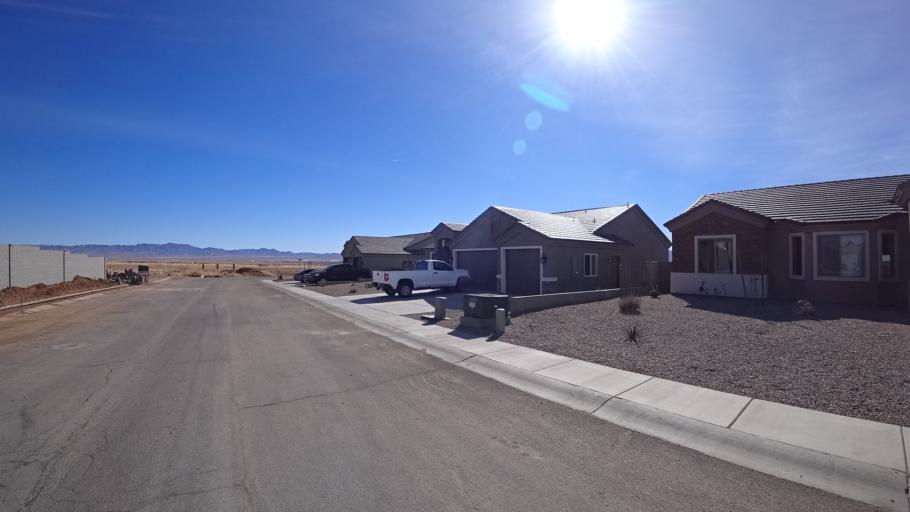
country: US
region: Arizona
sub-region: Mohave County
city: New Kingman-Butler
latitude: 35.2764
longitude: -114.0356
